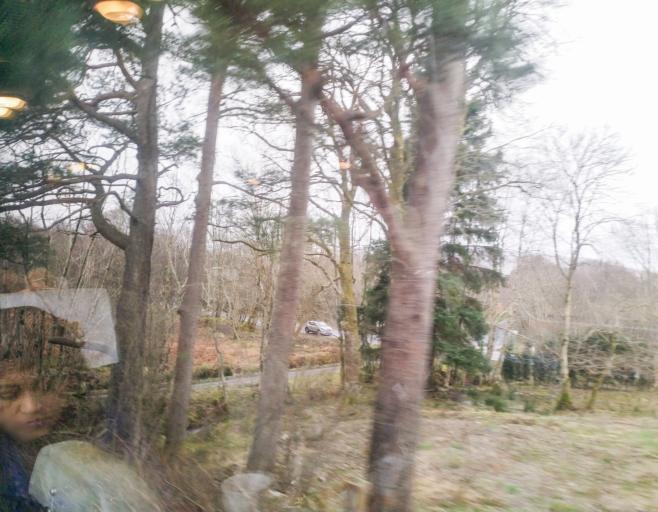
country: GB
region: Scotland
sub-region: Highland
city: Spean Bridge
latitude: 56.8867
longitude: -4.9419
